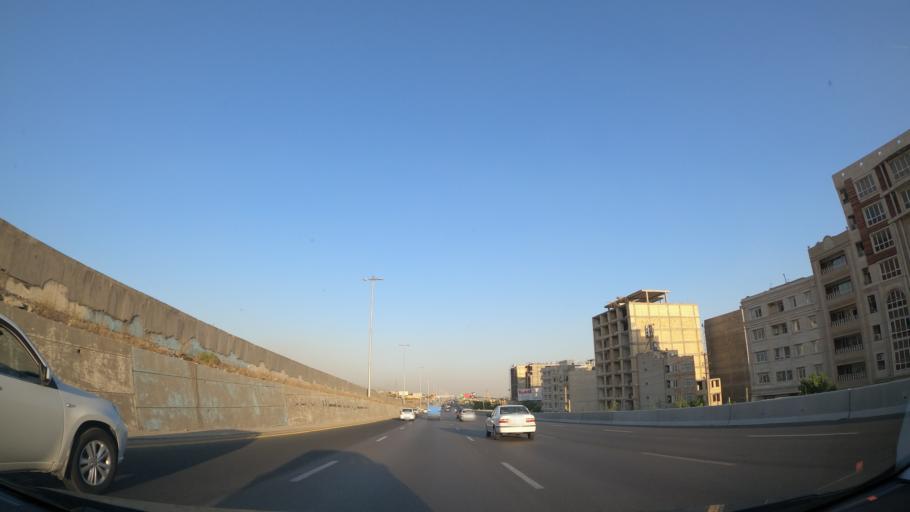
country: IR
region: Tehran
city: Shahr-e Qods
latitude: 35.7571
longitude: 51.0693
